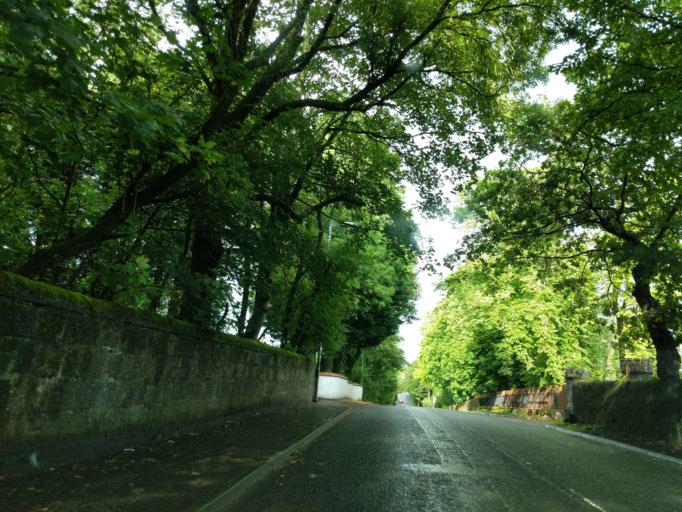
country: GB
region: Scotland
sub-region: East Renfrewshire
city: Barrhead
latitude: 55.8054
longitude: -4.3751
